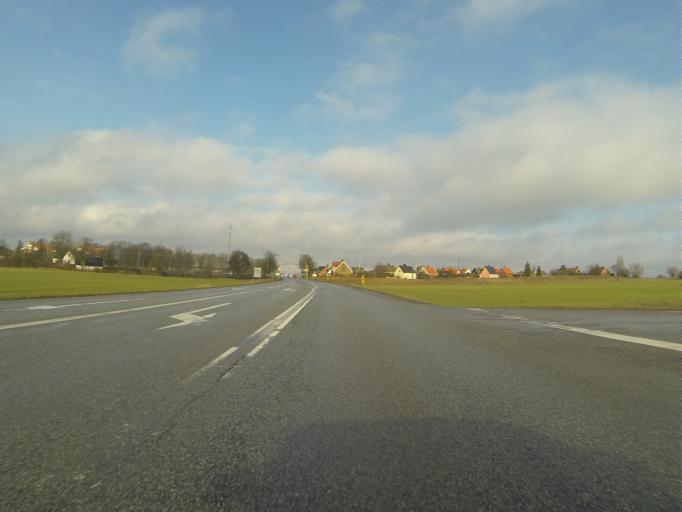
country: SE
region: Skane
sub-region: Svedala Kommun
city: Svedala
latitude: 55.5049
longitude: 13.2489
